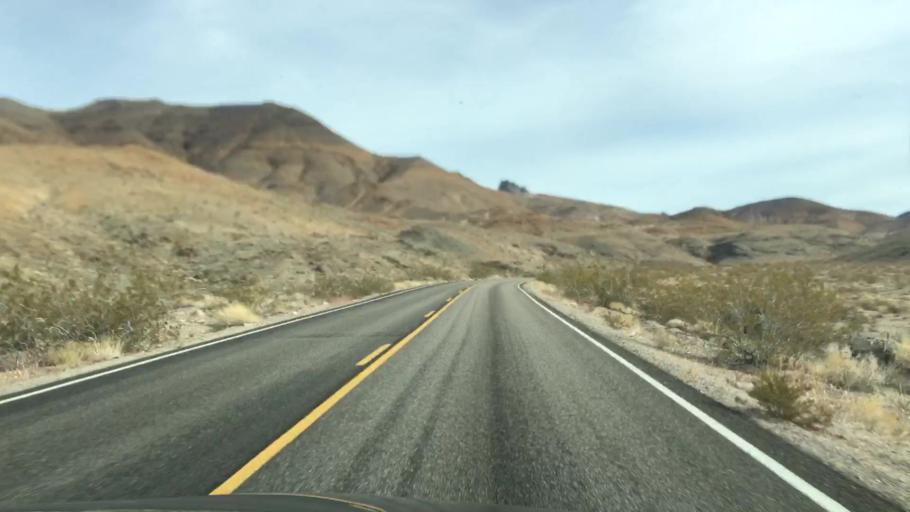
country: US
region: Nevada
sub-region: Nye County
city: Beatty
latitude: 36.7398
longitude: -116.9674
